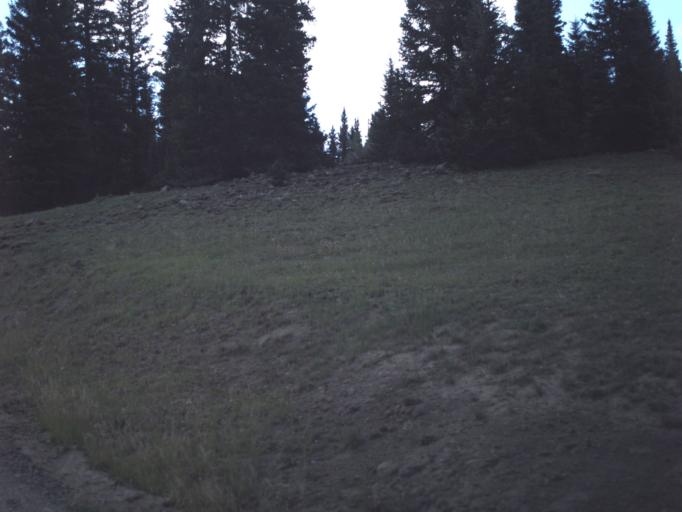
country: US
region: Utah
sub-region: Piute County
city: Junction
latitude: 38.2368
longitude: -112.3649
